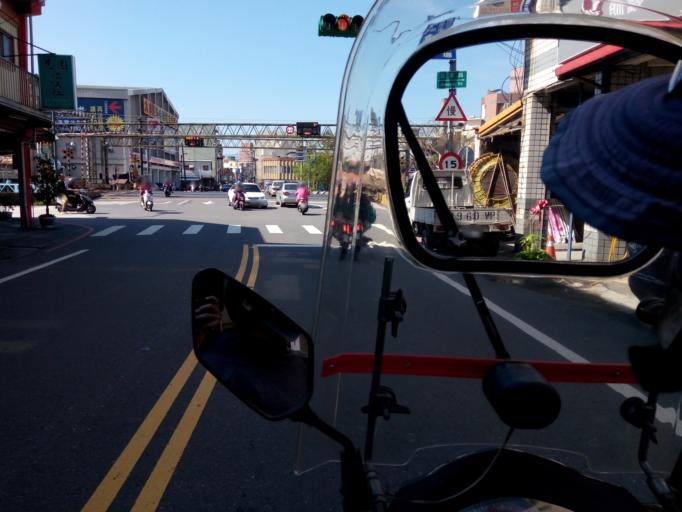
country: TW
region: Taiwan
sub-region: Yilan
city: Yilan
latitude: 24.6754
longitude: 121.7751
